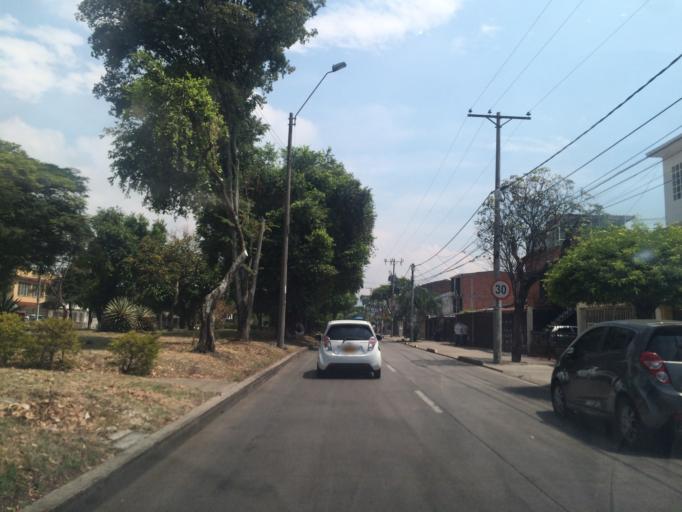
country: CO
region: Valle del Cauca
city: Cali
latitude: 3.4687
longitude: -76.5021
